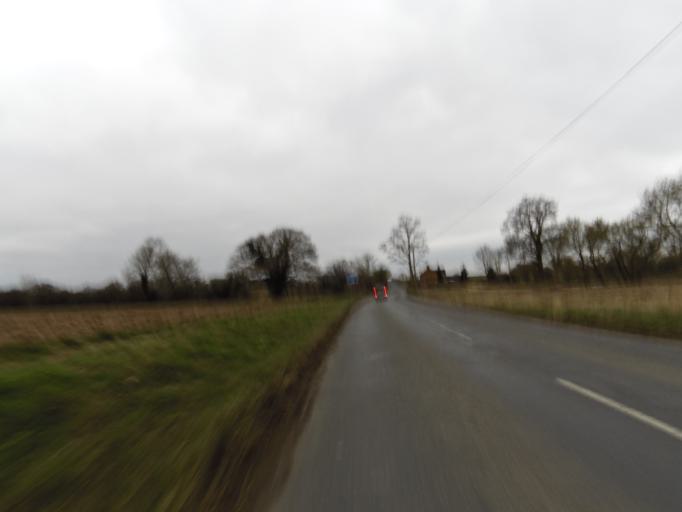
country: GB
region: England
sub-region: Suffolk
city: Ipswich
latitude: 52.1117
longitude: 1.1522
